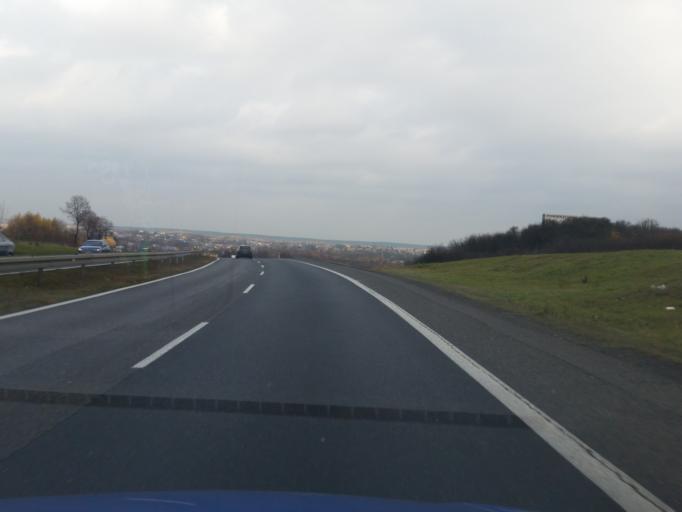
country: PL
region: Silesian Voivodeship
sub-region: Powiat myszkowski
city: Kozieglowy
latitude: 50.5828
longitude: 19.1642
